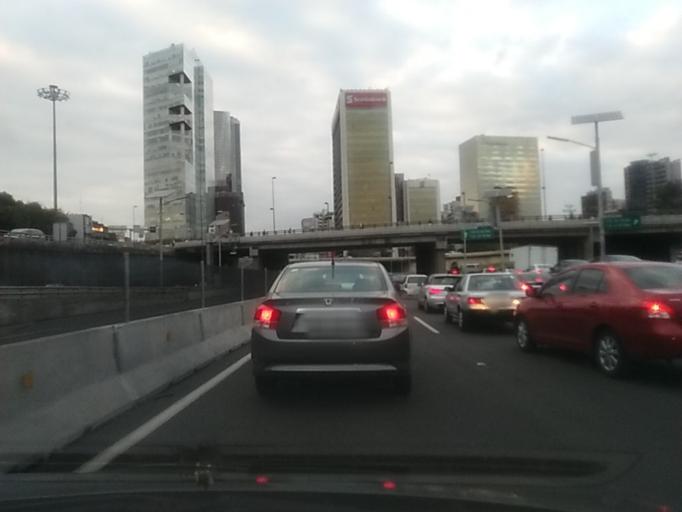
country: MX
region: Mexico City
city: Miguel Hidalgo
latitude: 19.4263
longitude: -99.2017
